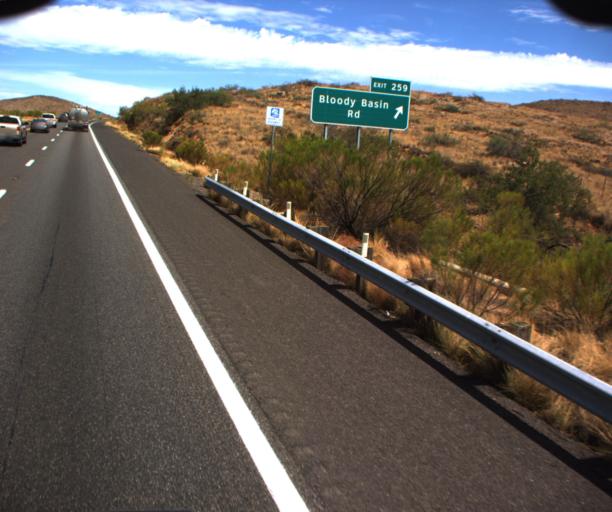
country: US
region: Arizona
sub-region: Yavapai County
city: Cordes Lakes
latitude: 34.2795
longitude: -112.1170
